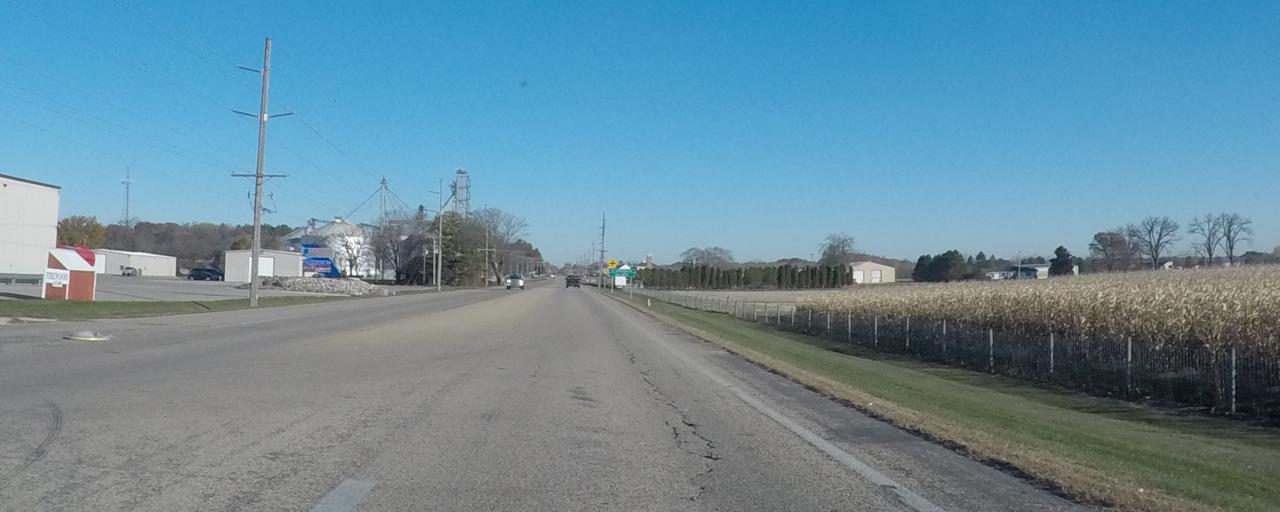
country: US
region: Wisconsin
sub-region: Dane County
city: Cottage Grove
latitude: 43.0619
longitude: -89.1997
